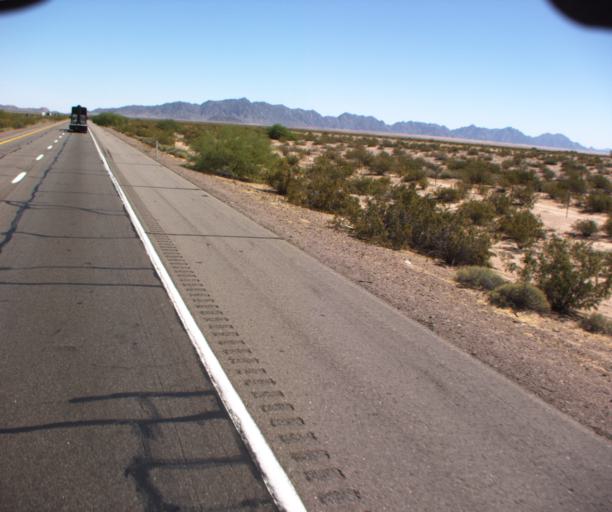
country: US
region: Arizona
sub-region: Yuma County
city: Wellton
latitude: 32.7067
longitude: -113.8653
